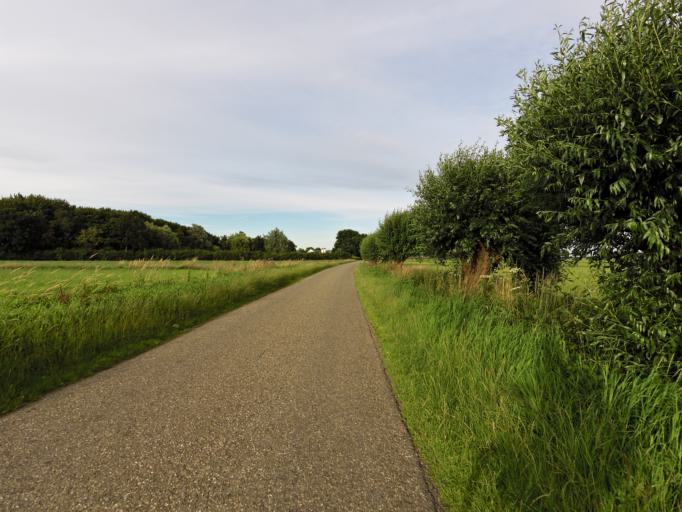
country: NL
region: Gelderland
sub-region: Gemeente Rheden
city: Rheden
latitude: 51.9749
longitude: 6.0624
